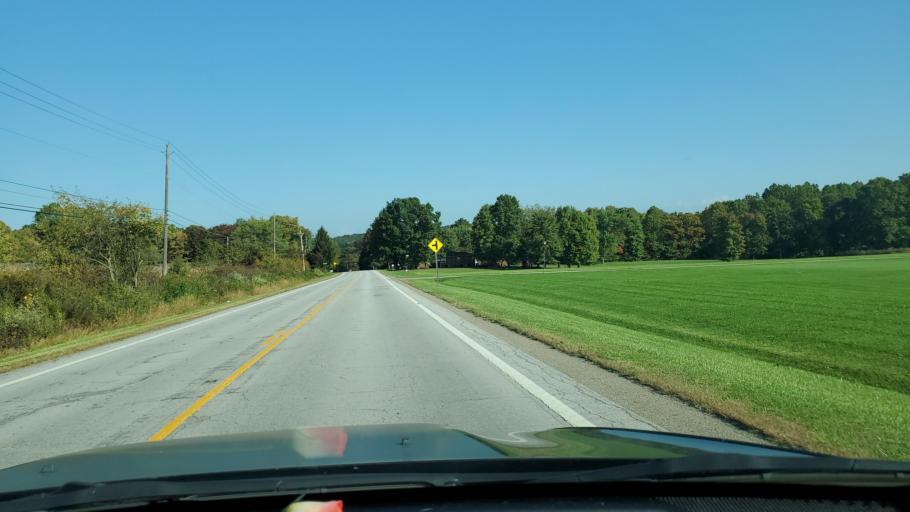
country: US
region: Ohio
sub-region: Trumbull County
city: Brookfield Center
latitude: 41.2623
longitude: -80.5682
